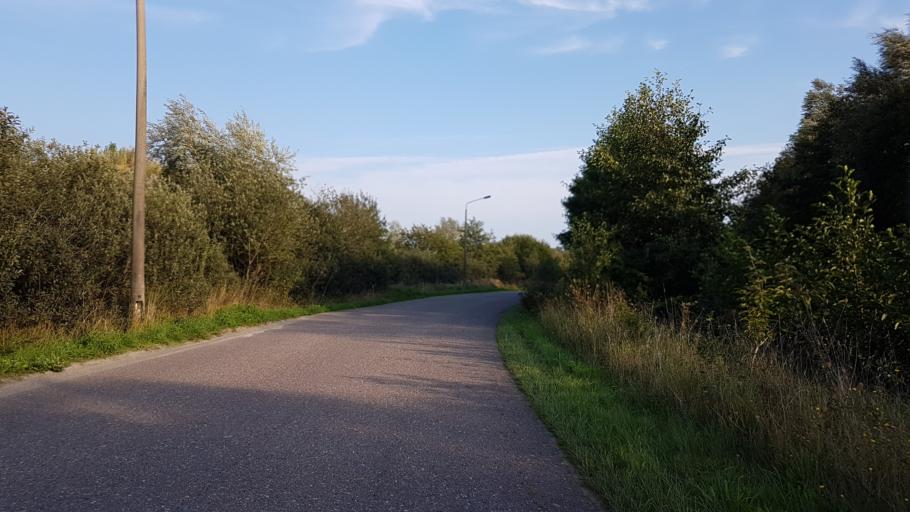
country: DE
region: Mecklenburg-Vorpommern
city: Sagard
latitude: 54.4967
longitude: 13.5514
